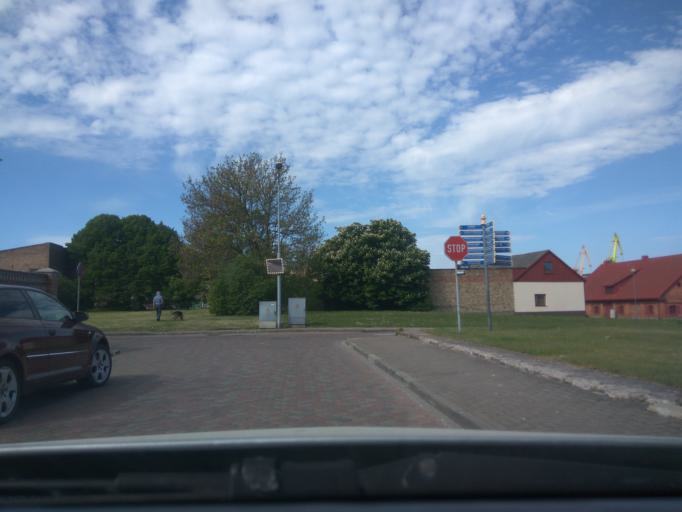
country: LV
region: Ventspils
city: Ventspils
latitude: 57.3975
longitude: 21.5654
